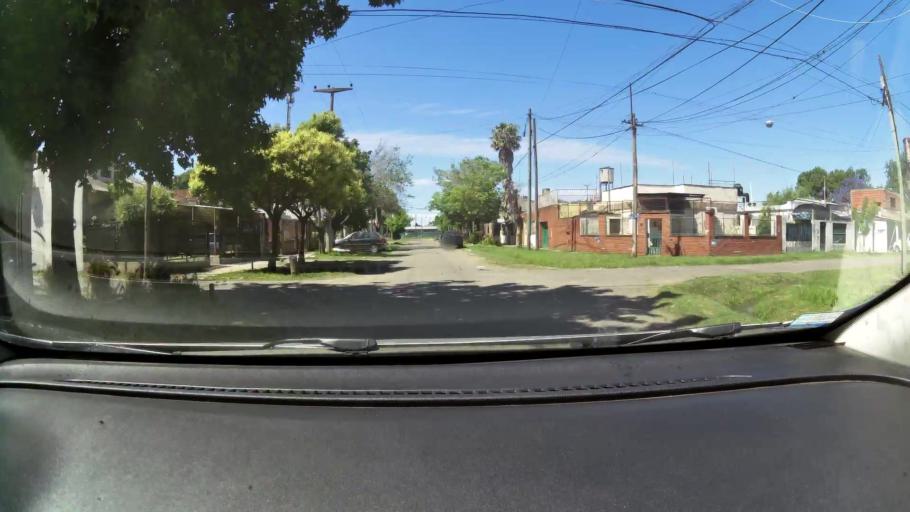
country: AR
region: Santa Fe
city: Perez
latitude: -32.9552
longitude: -60.7155
